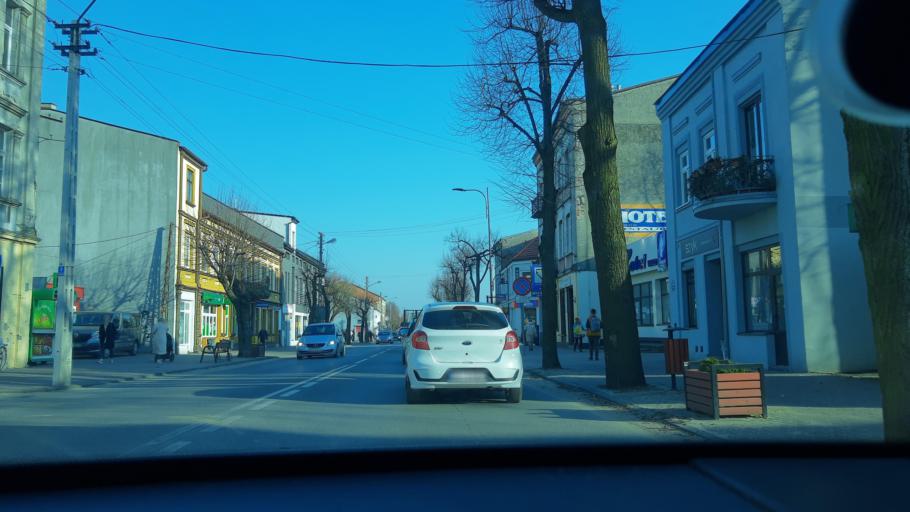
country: PL
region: Lodz Voivodeship
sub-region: Powiat zdunskowolski
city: Zdunska Wola
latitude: 51.6000
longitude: 18.9381
